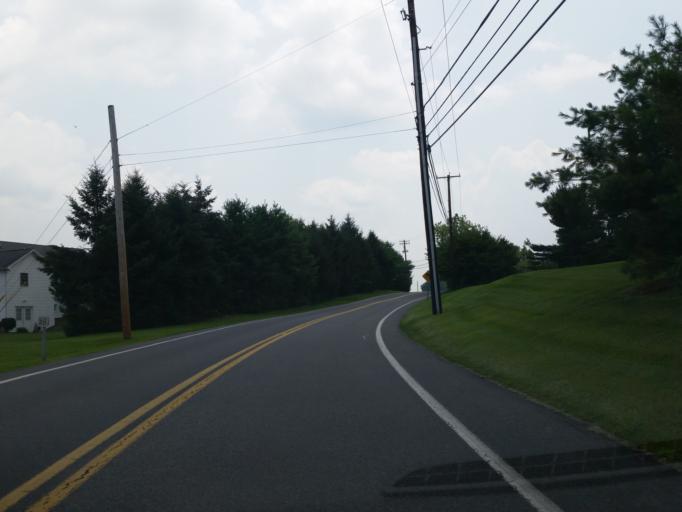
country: US
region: Pennsylvania
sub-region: Lebanon County
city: Palmyra
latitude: 40.2909
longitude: -76.6000
